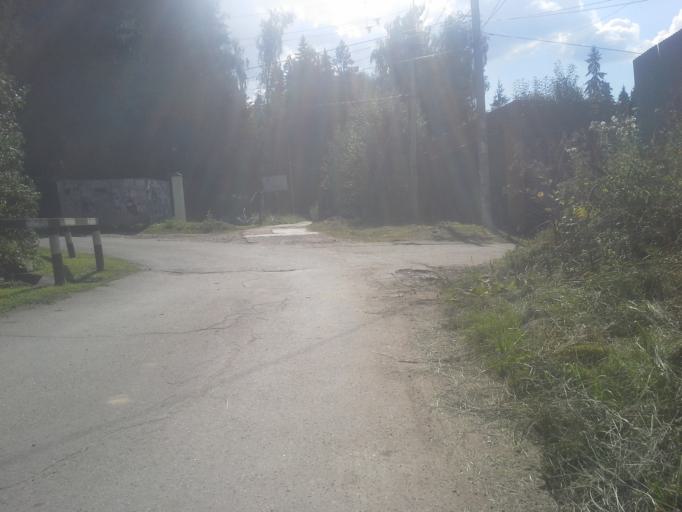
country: RU
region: Moskovskaya
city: Selyatino
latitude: 55.4654
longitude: 36.9906
